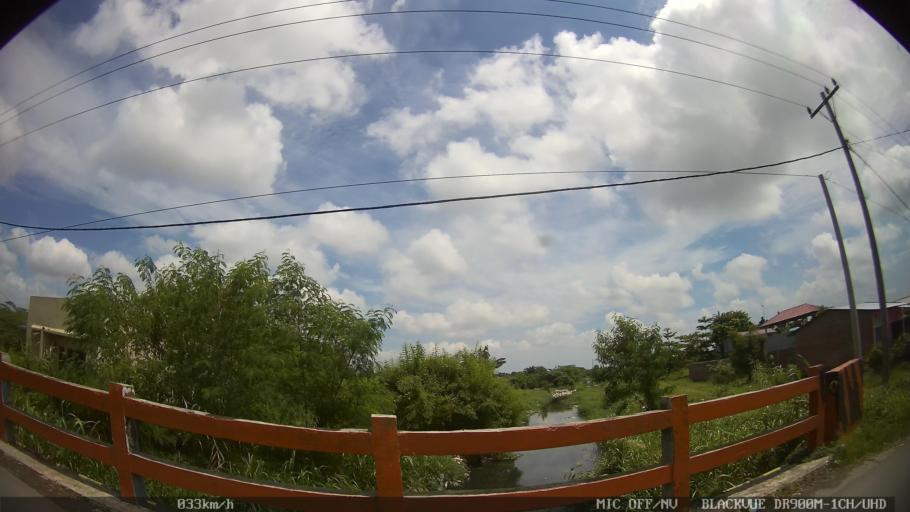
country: ID
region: North Sumatra
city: Percut
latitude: 3.6197
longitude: 98.7727
